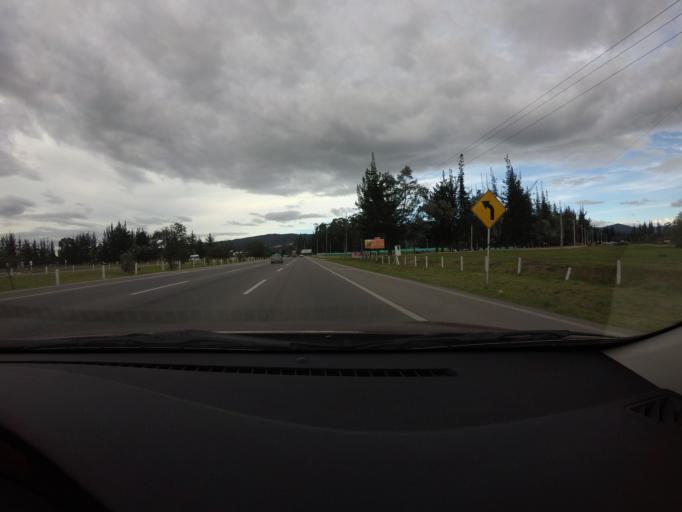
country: CO
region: Cundinamarca
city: Sopo
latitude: 4.9389
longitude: -73.9655
